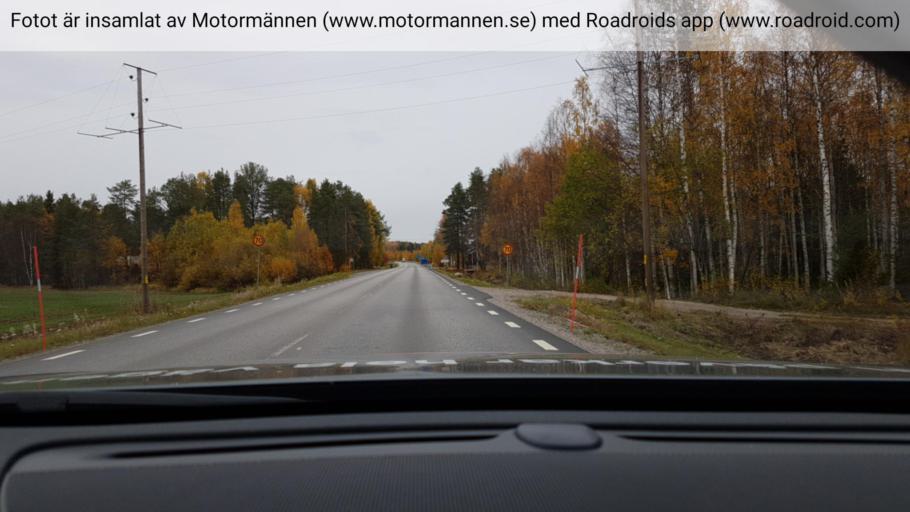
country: SE
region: Norrbotten
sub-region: Overkalix Kommun
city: OEverkalix
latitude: 66.3588
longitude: 22.8338
